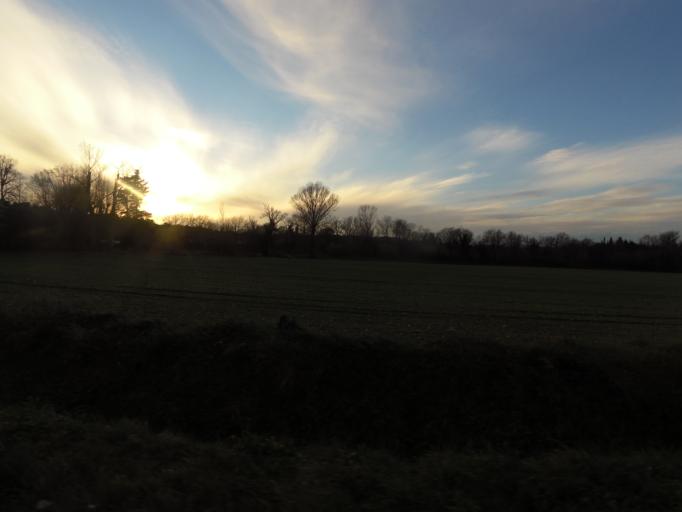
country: FR
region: Languedoc-Roussillon
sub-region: Departement du Gard
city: Saint-Mamert-du-Gard
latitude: 43.8693
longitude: 4.2135
